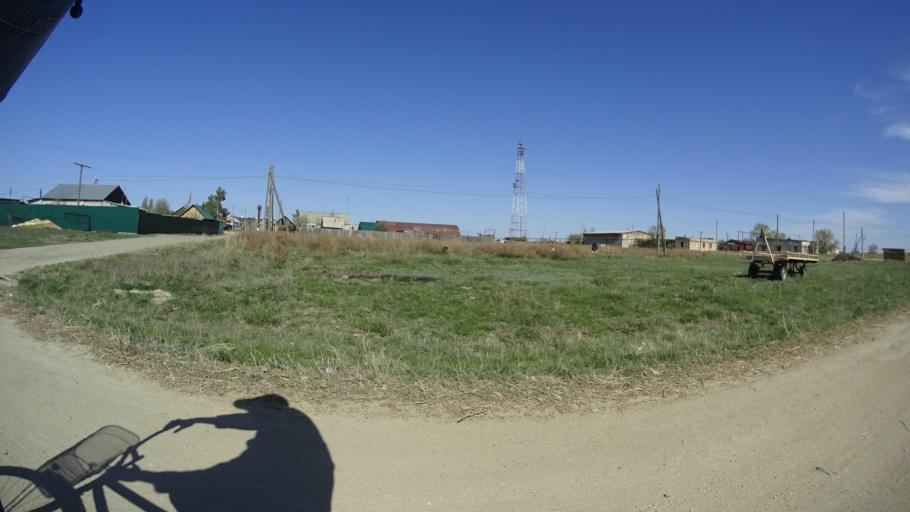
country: RU
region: Chelyabinsk
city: Chesma
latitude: 53.7891
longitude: 61.0380
